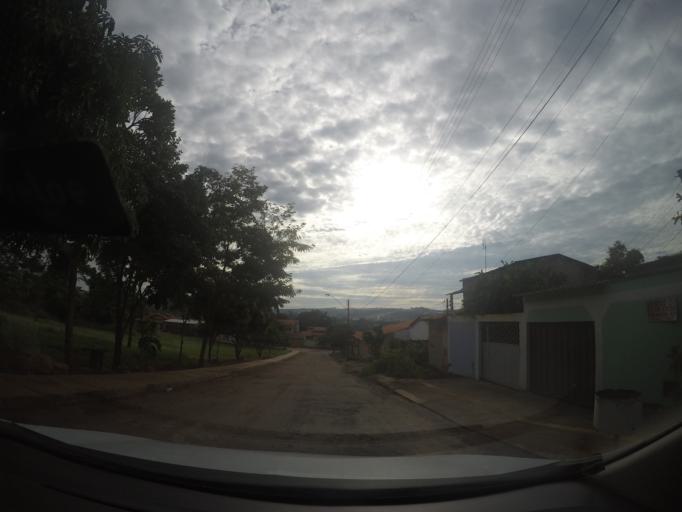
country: BR
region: Goias
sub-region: Goiania
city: Goiania
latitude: -16.6886
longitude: -49.2014
